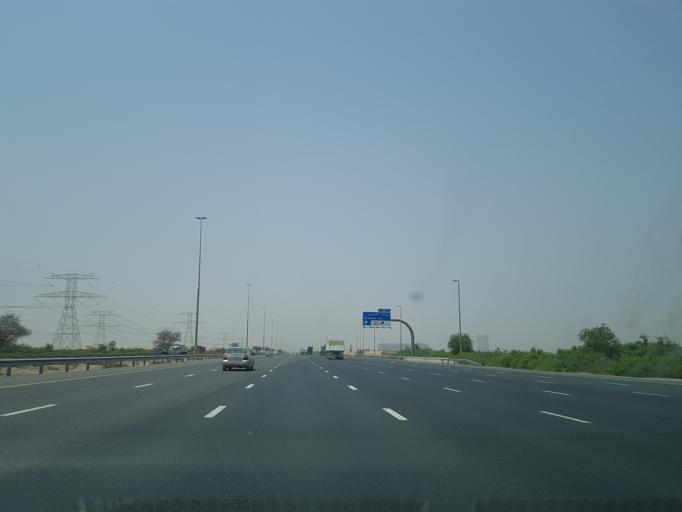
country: AE
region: Ash Shariqah
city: Sharjah
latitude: 25.1053
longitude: 55.4181
